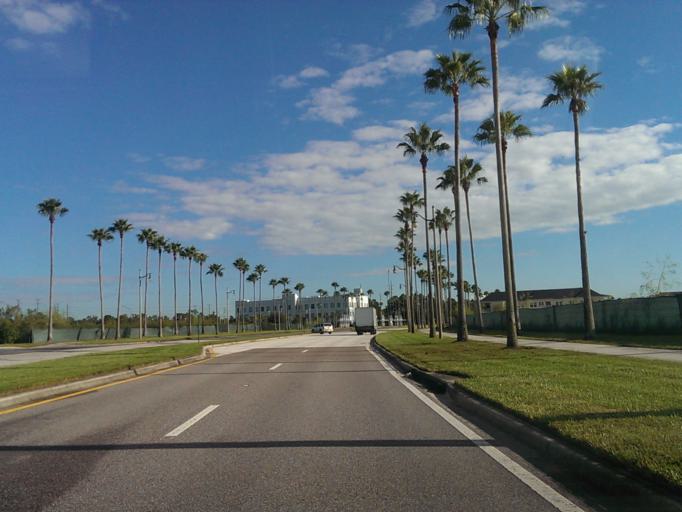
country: US
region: Florida
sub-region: Osceola County
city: Celebration
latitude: 28.3095
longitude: -81.5637
